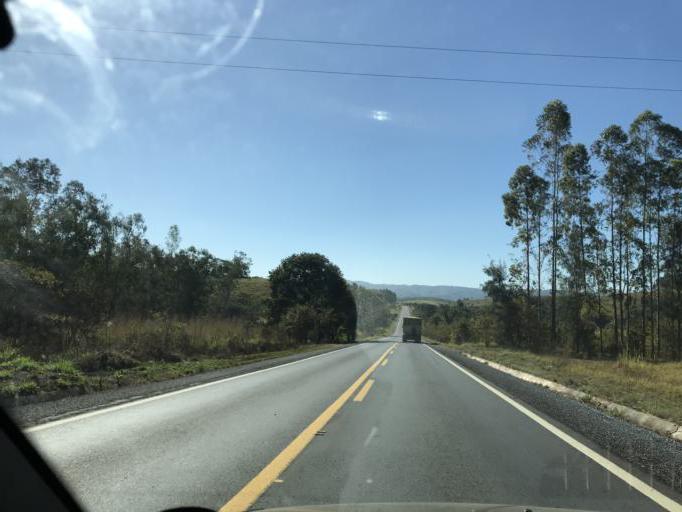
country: BR
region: Minas Gerais
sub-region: Bambui
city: Bambui
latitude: -19.8645
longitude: -45.9856
